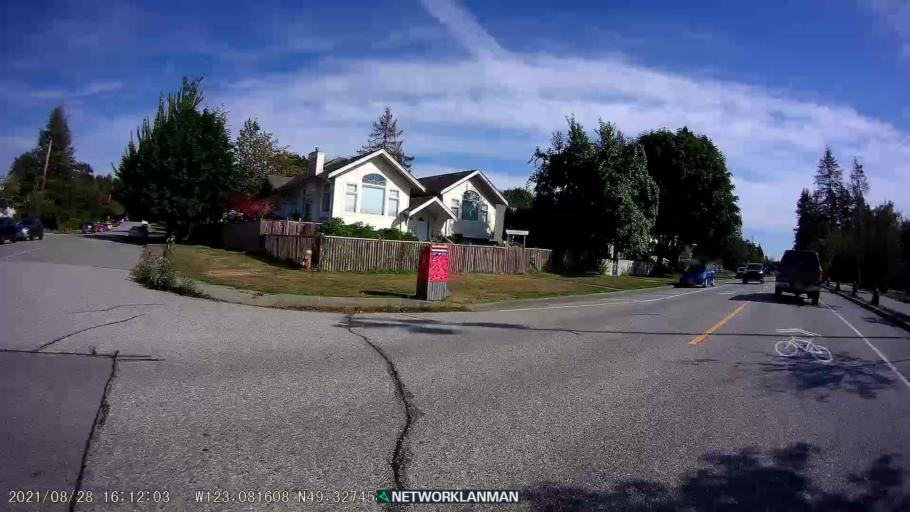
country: CA
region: British Columbia
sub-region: Fraser Valley Regional District
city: North Vancouver
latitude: 49.3272
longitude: -123.0816
